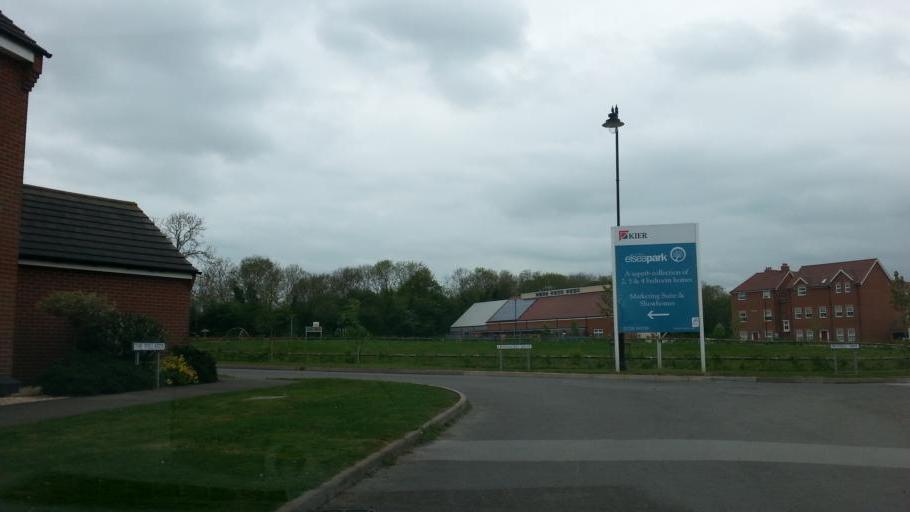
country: GB
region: England
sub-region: Lincolnshire
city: Bourne
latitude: 52.7585
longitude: -0.3771
